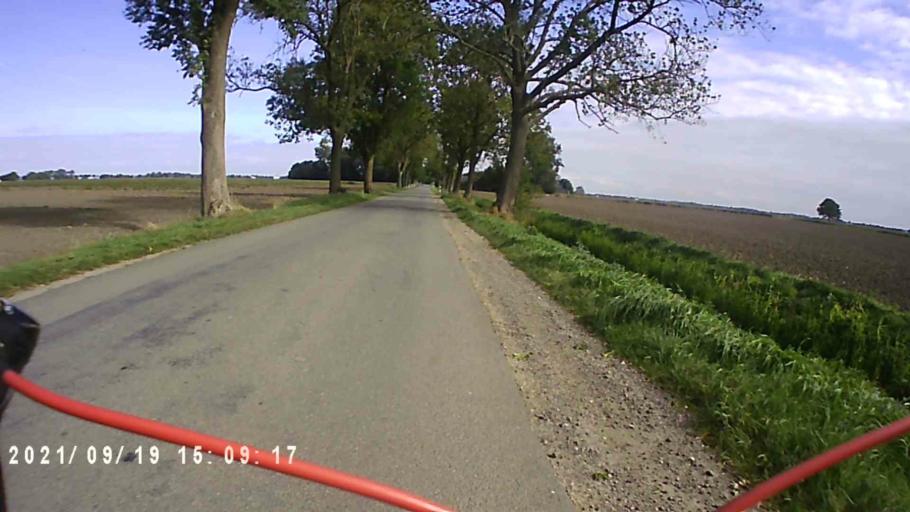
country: DE
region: Lower Saxony
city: Bunde
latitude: 53.1717
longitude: 7.2252
